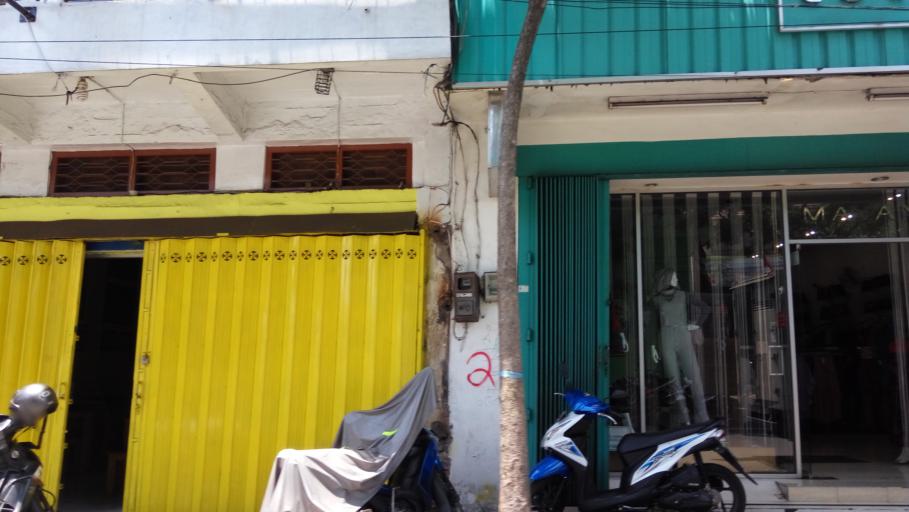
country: ID
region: East Java
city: Malang
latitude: -7.9836
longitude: 112.6264
